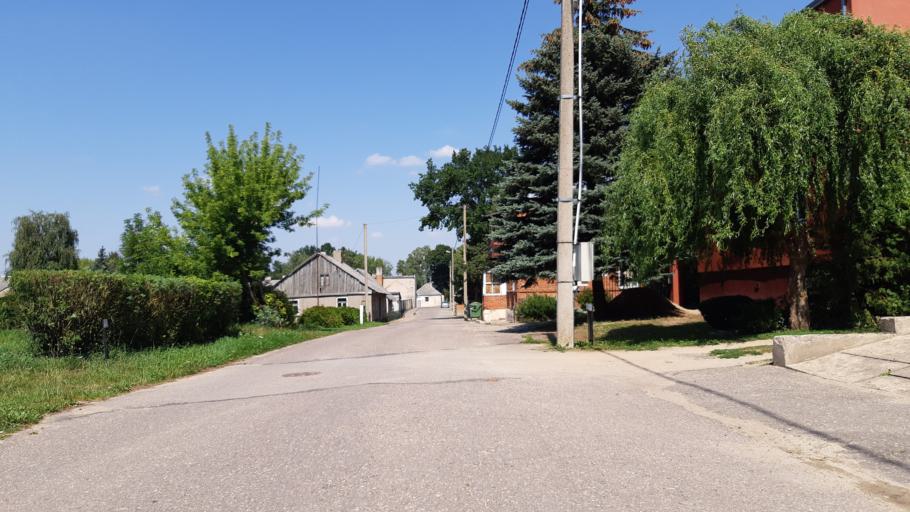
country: LT
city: Virbalis
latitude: 54.6242
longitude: 22.8210
